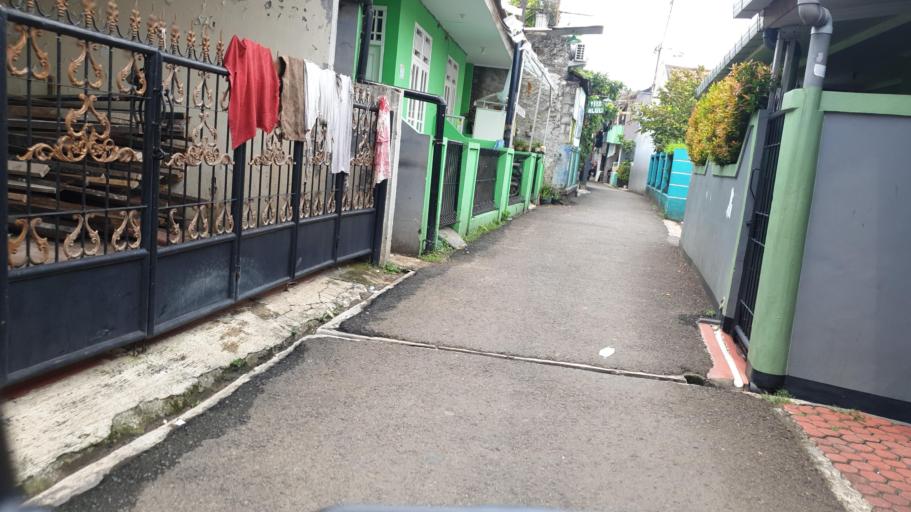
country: ID
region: West Java
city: Depok
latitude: -6.3365
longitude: 106.8227
